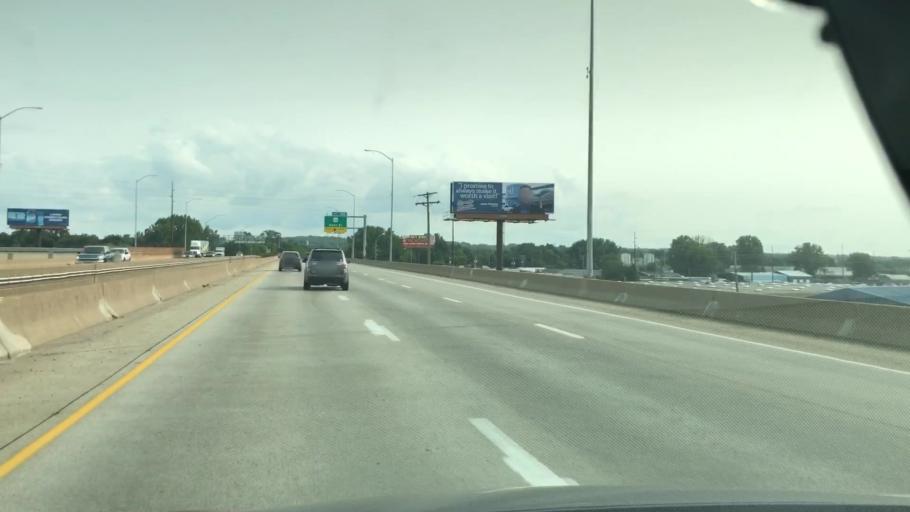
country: US
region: Pennsylvania
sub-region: Erie County
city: Erie
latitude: 42.1030
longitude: -80.1222
